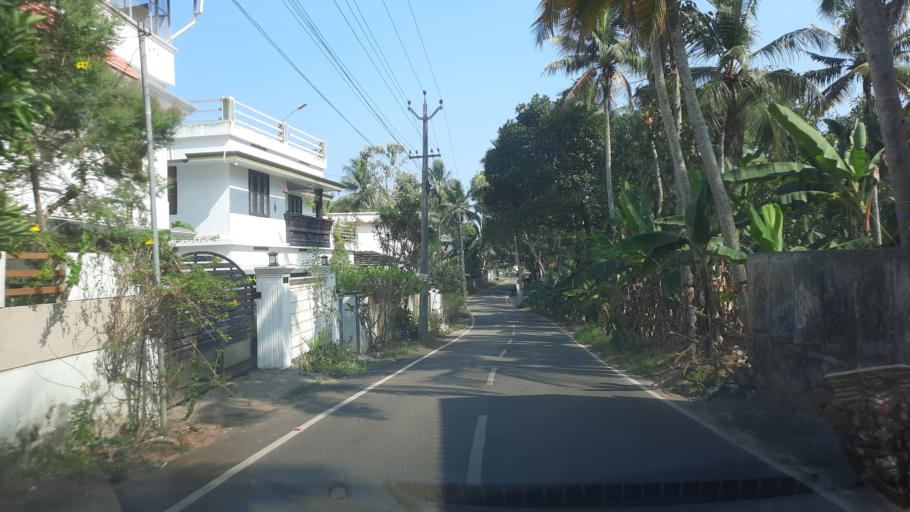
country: IN
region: Kerala
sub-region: Thiruvananthapuram
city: Nedumangad
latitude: 8.5892
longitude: 76.9309
